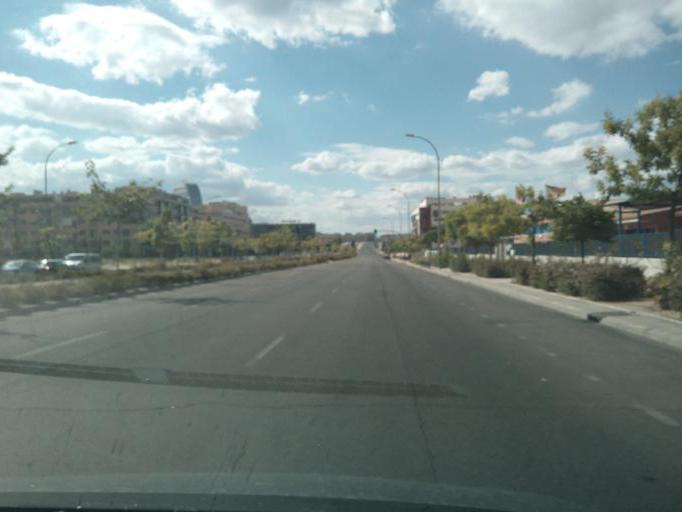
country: ES
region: Madrid
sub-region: Provincia de Madrid
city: Las Tablas
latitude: 40.4985
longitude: -3.6555
